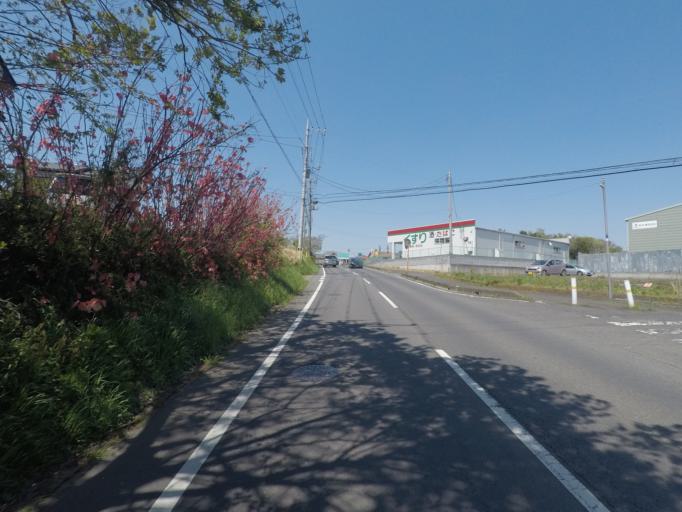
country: JP
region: Ibaraki
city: Ushiku
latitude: 35.9584
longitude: 140.1035
